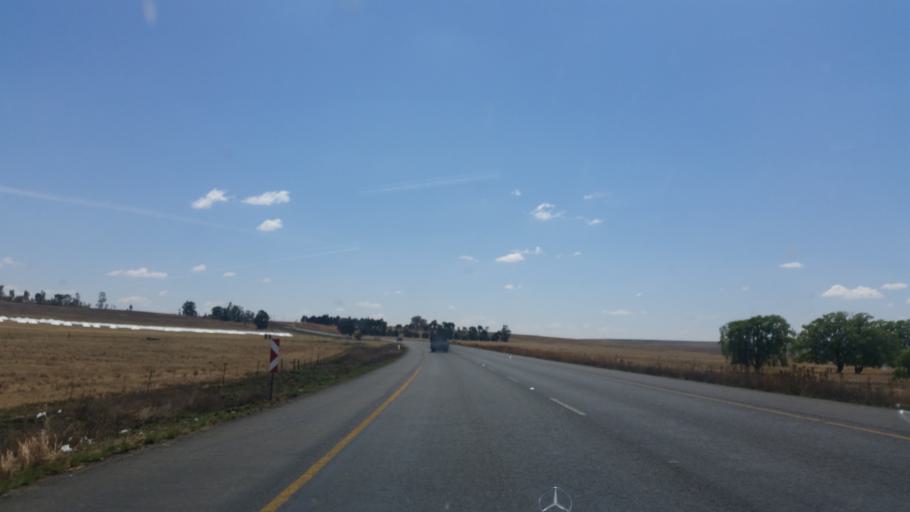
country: ZA
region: Orange Free State
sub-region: Thabo Mofutsanyana District Municipality
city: Bethlehem
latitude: -28.1216
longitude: 28.6817
